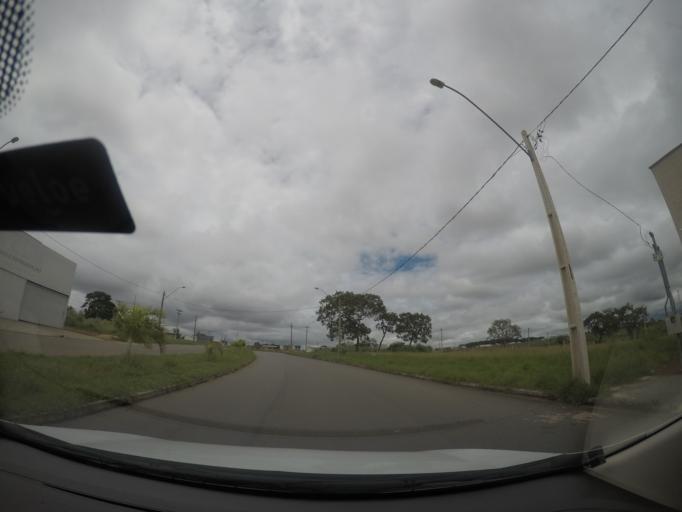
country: BR
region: Goias
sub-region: Goiania
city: Goiania
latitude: -16.7472
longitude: -49.3374
